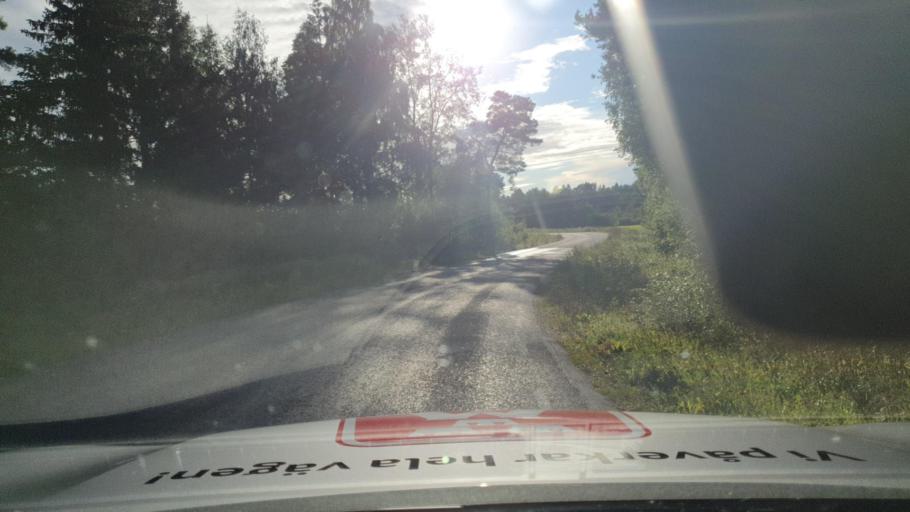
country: SE
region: Gotland
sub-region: Gotland
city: Hemse
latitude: 57.4191
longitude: 18.5696
